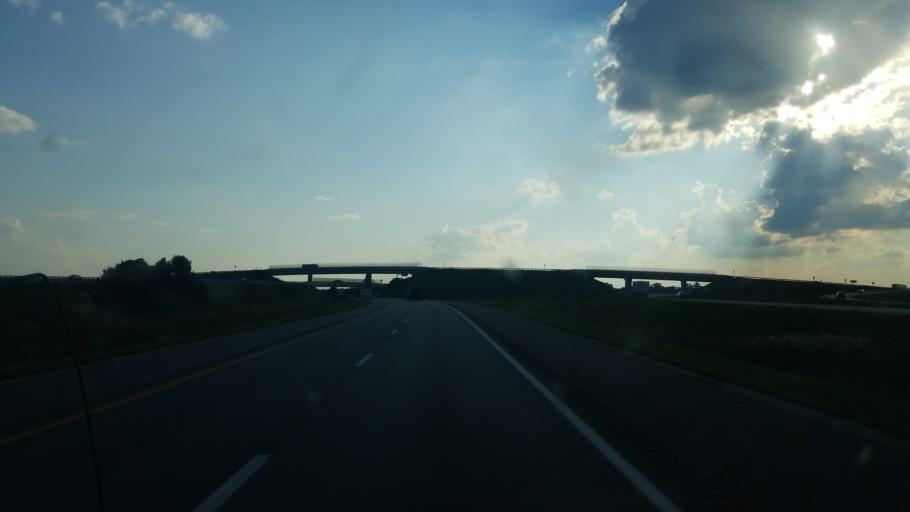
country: US
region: Ohio
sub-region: Wood County
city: Perrysburg
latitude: 41.5347
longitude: -83.6190
